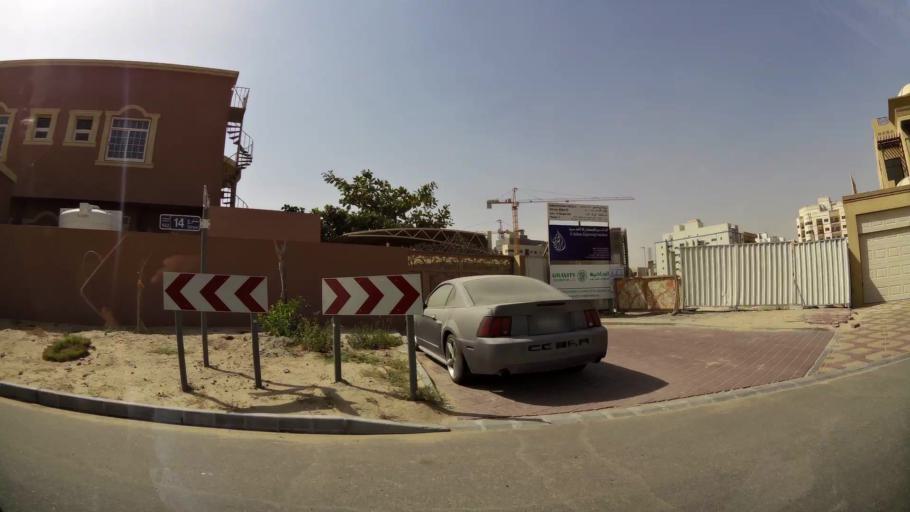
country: AE
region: Ash Shariqah
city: Sharjah
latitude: 25.1972
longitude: 55.4029
